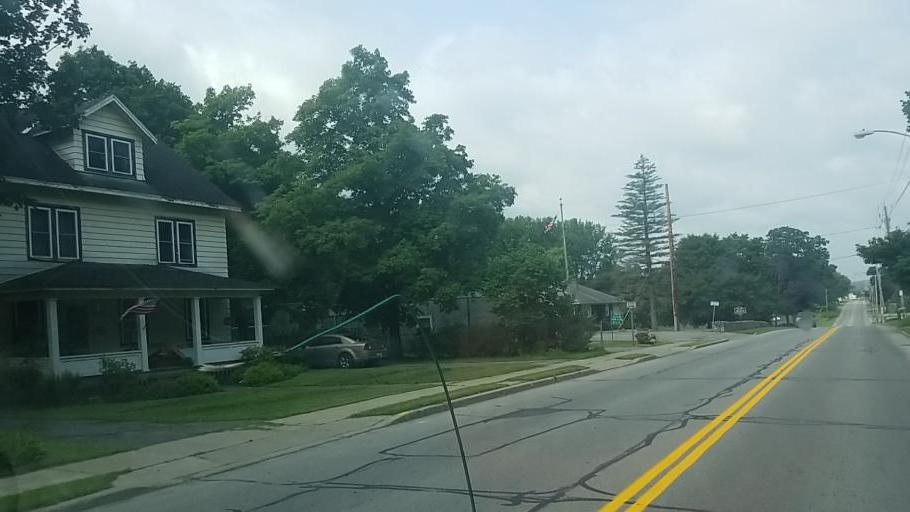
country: US
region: New York
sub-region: Montgomery County
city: Canajoharie
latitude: 42.9130
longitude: -74.5811
